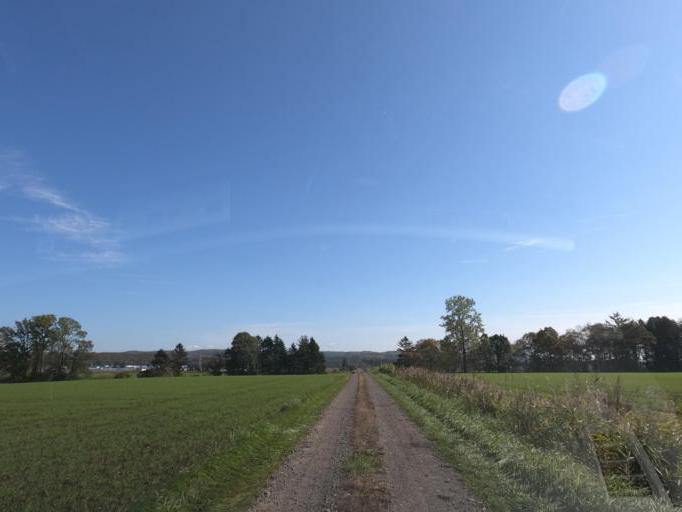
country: JP
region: Hokkaido
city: Obihiro
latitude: 42.9545
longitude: 143.2355
